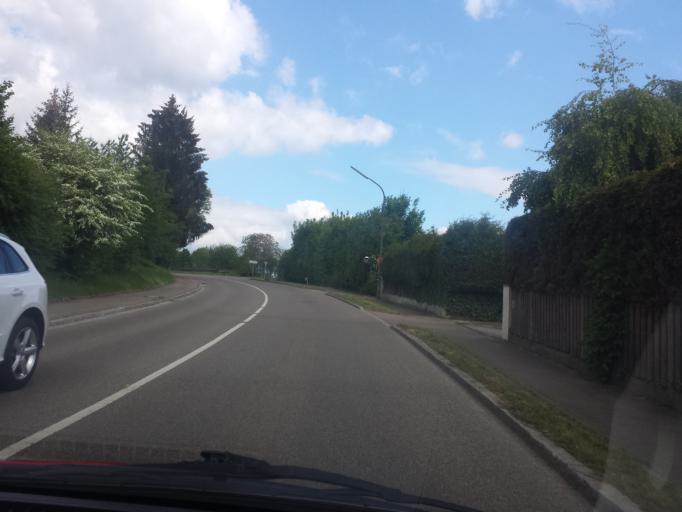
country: DE
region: Bavaria
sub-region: Upper Bavaria
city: Hepberg
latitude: 48.8084
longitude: 11.4641
